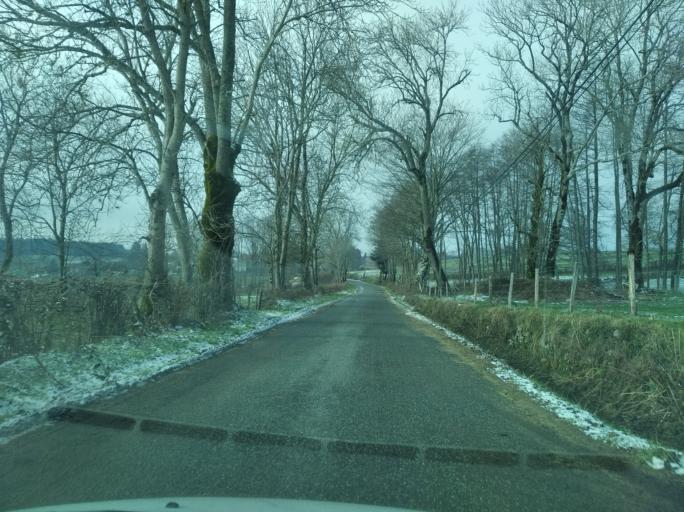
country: FR
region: Rhone-Alpes
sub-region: Departement de la Loire
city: Ambierle
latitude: 46.1140
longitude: 3.8020
